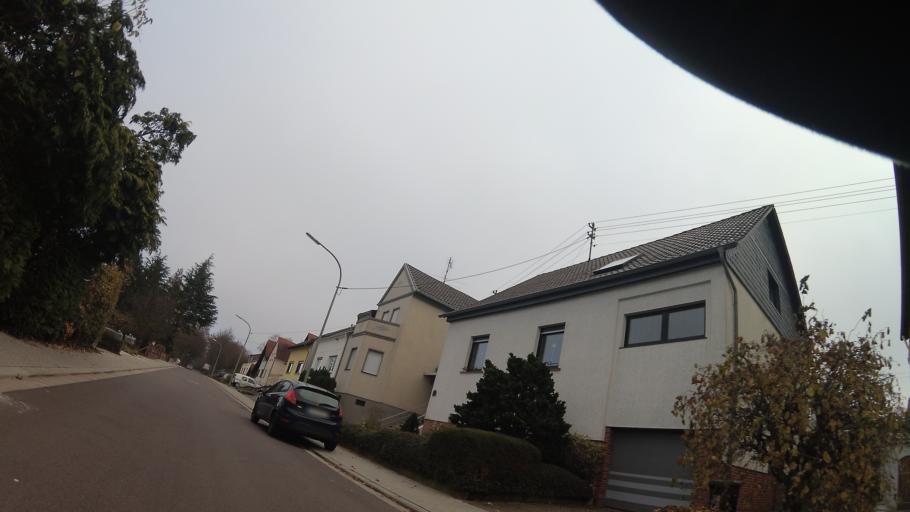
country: DE
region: Saarland
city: Schwalbach
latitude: 49.2954
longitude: 6.8062
